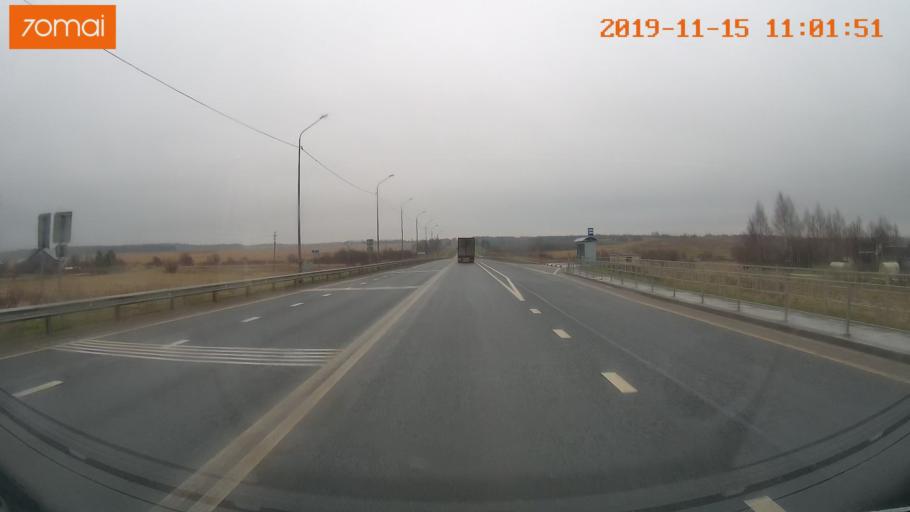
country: RU
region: Vologda
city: Chebsara
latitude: 59.1312
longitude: 38.9287
